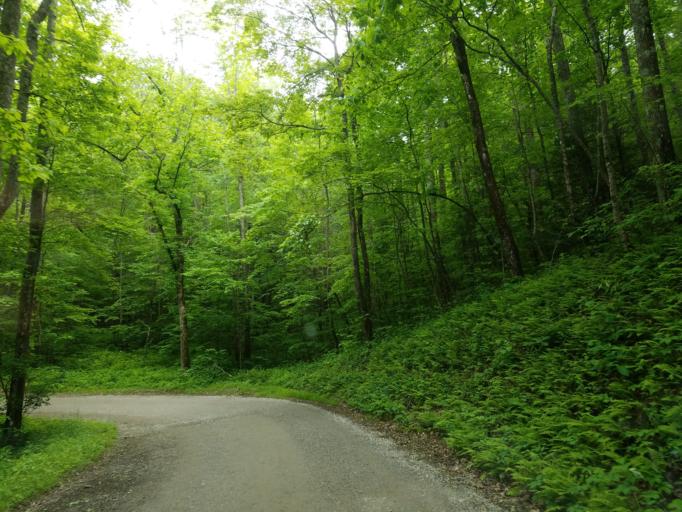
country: US
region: Georgia
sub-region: Union County
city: Blairsville
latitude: 34.7325
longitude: -83.9722
